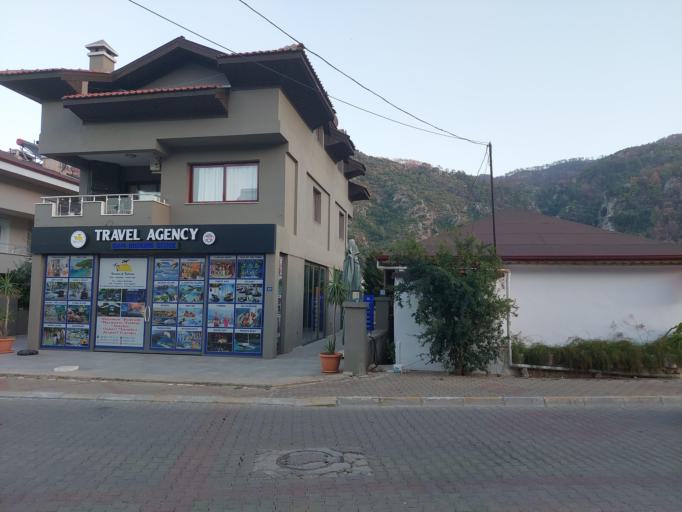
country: TR
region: Mugla
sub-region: Marmaris
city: Marmaris
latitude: 36.7977
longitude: 28.2263
